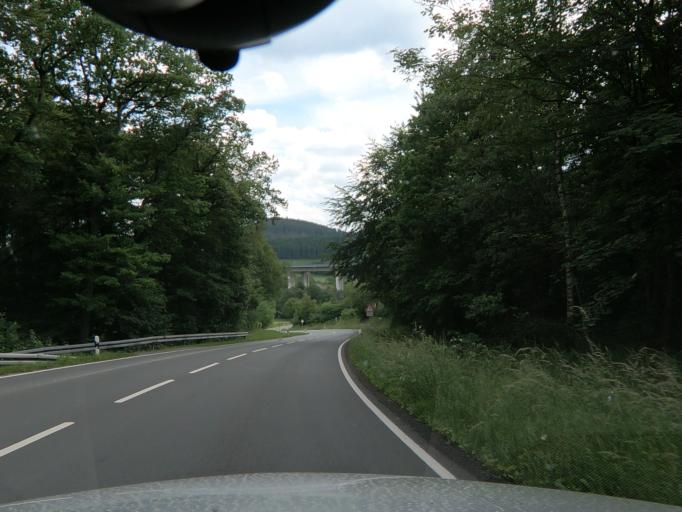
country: DE
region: North Rhine-Westphalia
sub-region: Regierungsbezirk Arnsberg
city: Meschede
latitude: 51.3685
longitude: 8.3033
